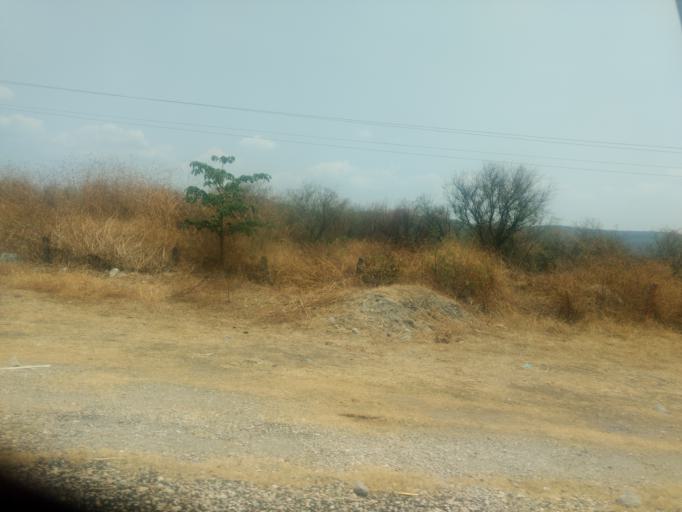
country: MX
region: Morelos
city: La Joya
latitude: 18.6841
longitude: -99.4423
